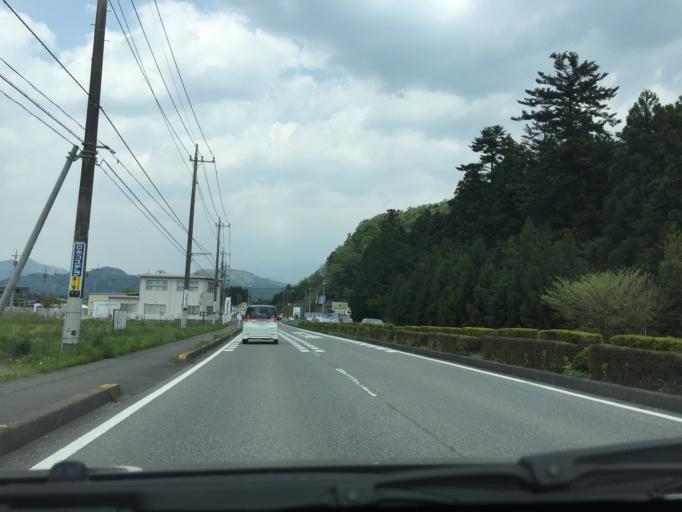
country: JP
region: Tochigi
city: Imaichi
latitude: 36.7511
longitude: 139.7146
